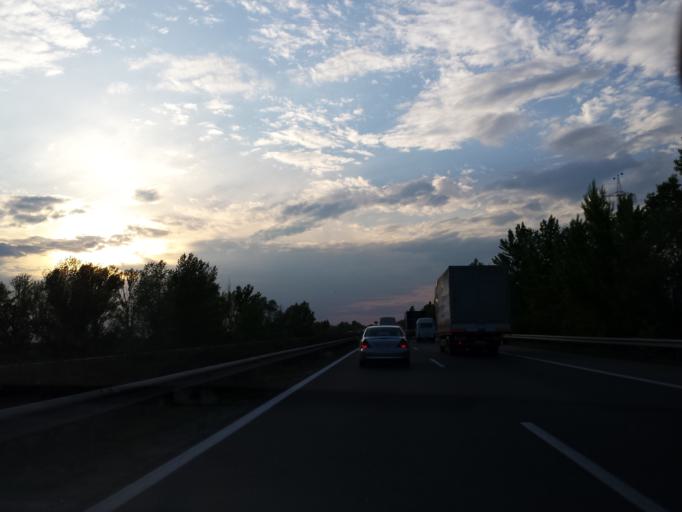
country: HU
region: Gyor-Moson-Sopron
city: Abda
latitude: 47.6612
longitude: 17.5838
